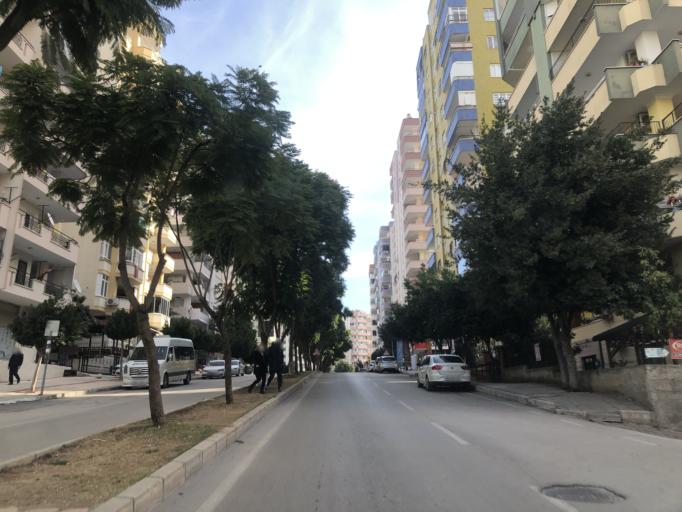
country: TR
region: Adana
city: Seyhan
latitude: 37.0526
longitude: 35.2798
